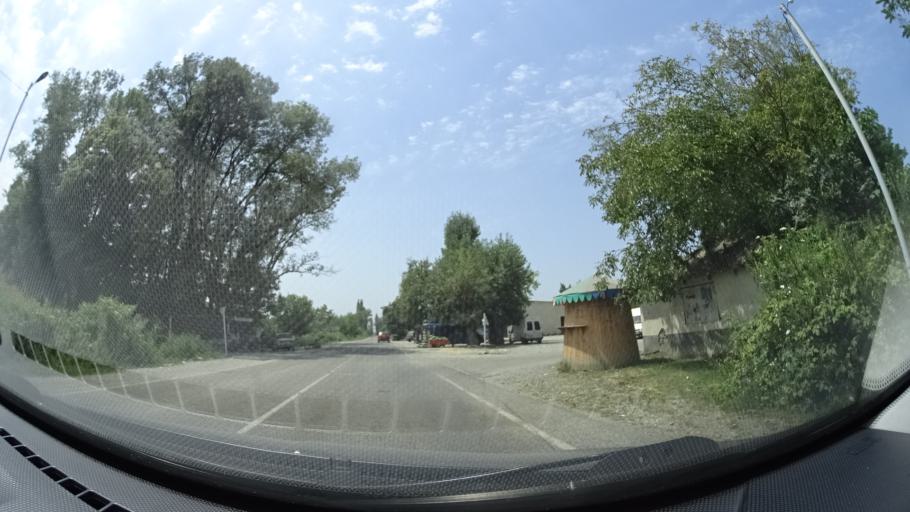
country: GE
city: Bagdadi
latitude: 41.7607
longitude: 46.1170
